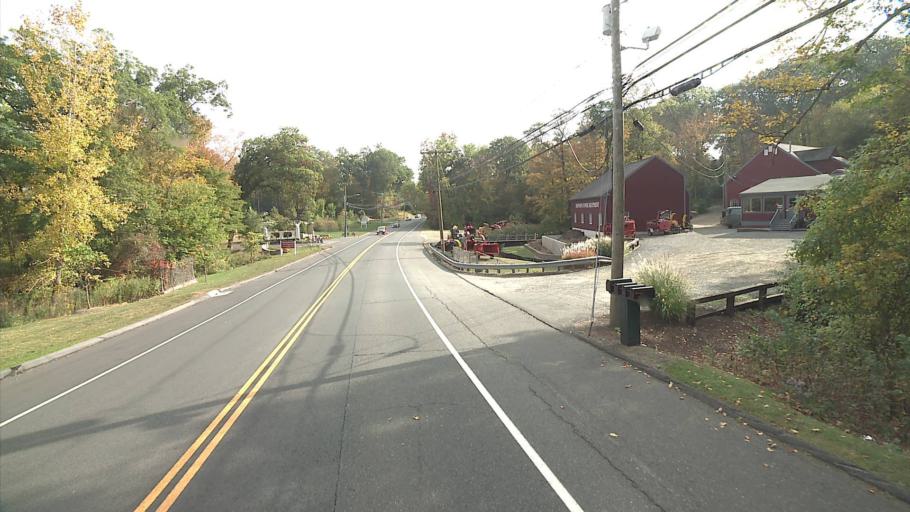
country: US
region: Connecticut
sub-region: Fairfield County
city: Newtown
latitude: 41.4157
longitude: -73.3672
